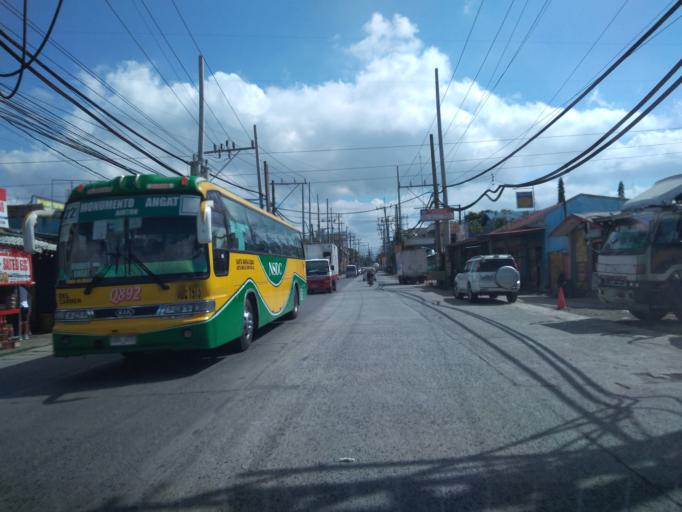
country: PH
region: Central Luzon
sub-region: Province of Bulacan
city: Bocaue
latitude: 14.8077
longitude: 120.9418
